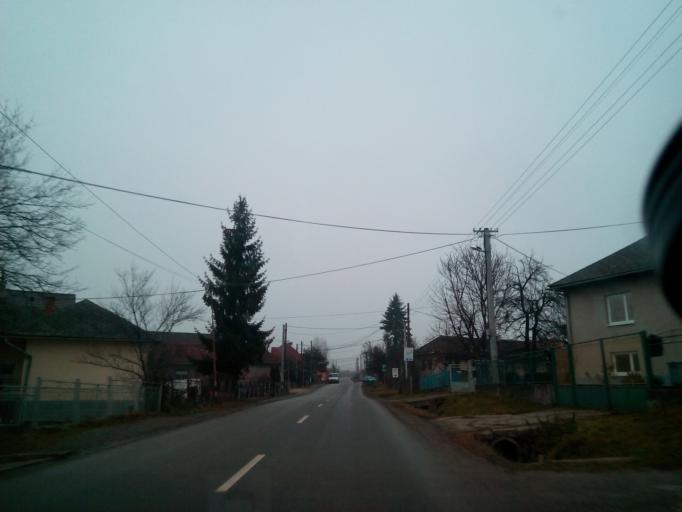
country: SK
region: Kosicky
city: Krompachy
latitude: 48.9668
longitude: 20.9547
